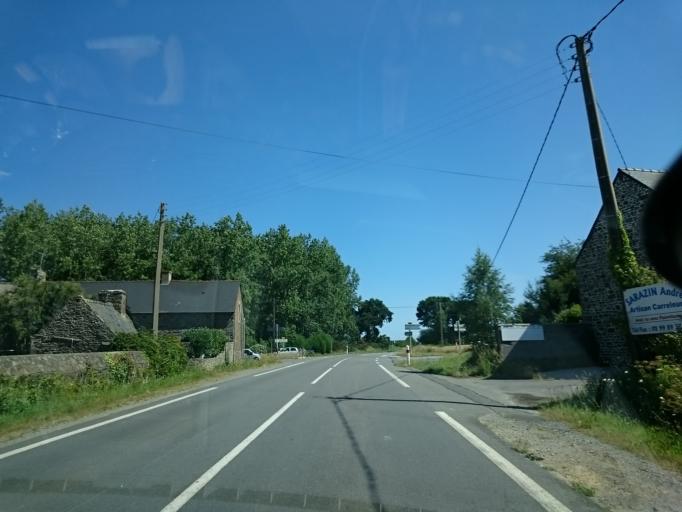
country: FR
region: Brittany
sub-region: Departement d'Ille-et-Vilaine
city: Saint-Pere
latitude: 48.5858
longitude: -1.9085
